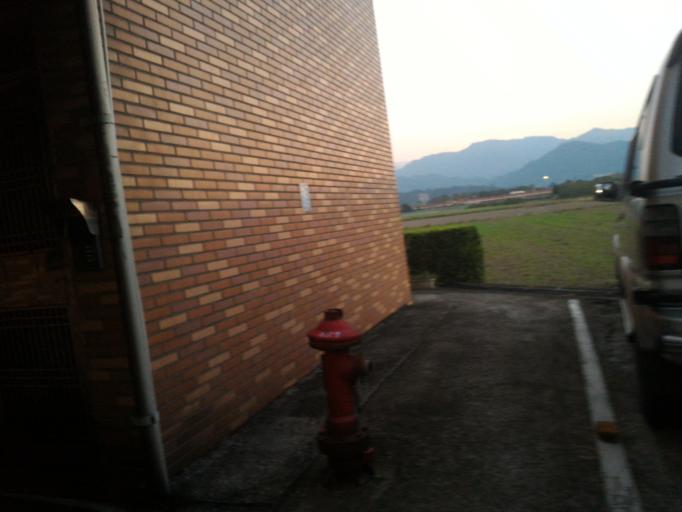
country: TW
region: Taiwan
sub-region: Taoyuan
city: Taoyuan
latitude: 24.9557
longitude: 121.3918
